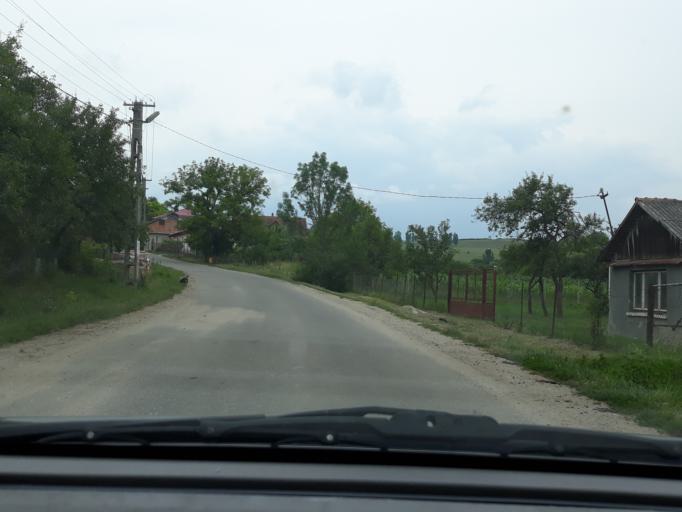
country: RO
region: Salaj
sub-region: Comuna Criseni
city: Criseni
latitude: 47.2559
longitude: 23.0630
